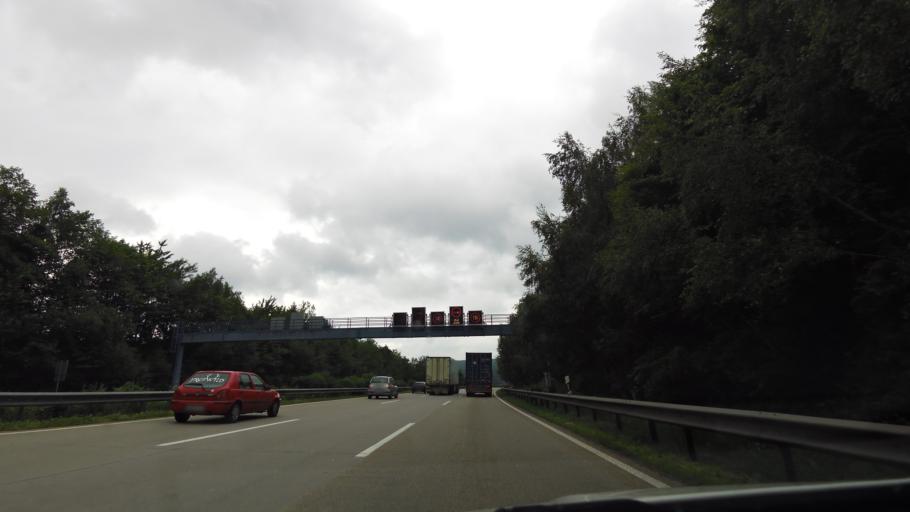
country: DE
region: Rheinland-Pfalz
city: Waldorf
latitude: 50.4942
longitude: 7.2236
